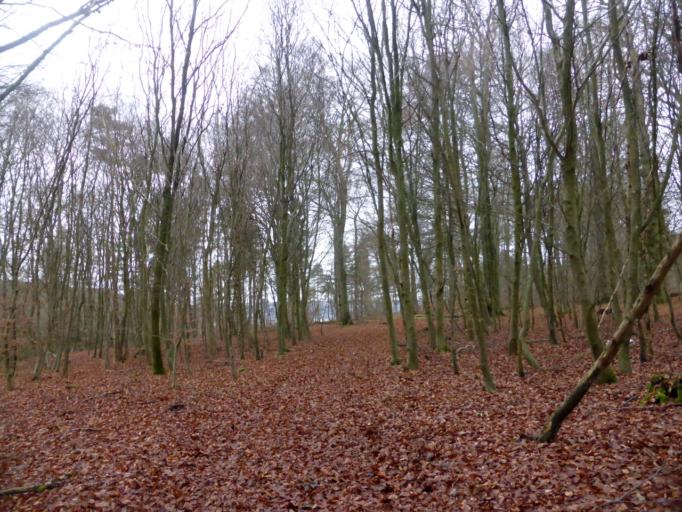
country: LU
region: Luxembourg
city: Heisdorf-sur-Alzette
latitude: 49.6766
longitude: 6.1563
